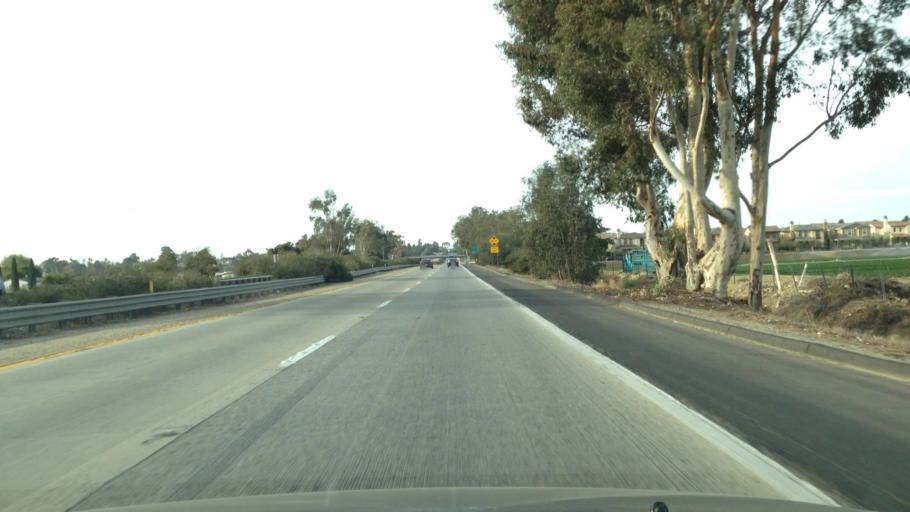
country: US
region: California
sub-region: Ventura County
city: Saticoy
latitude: 34.2951
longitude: -119.1474
